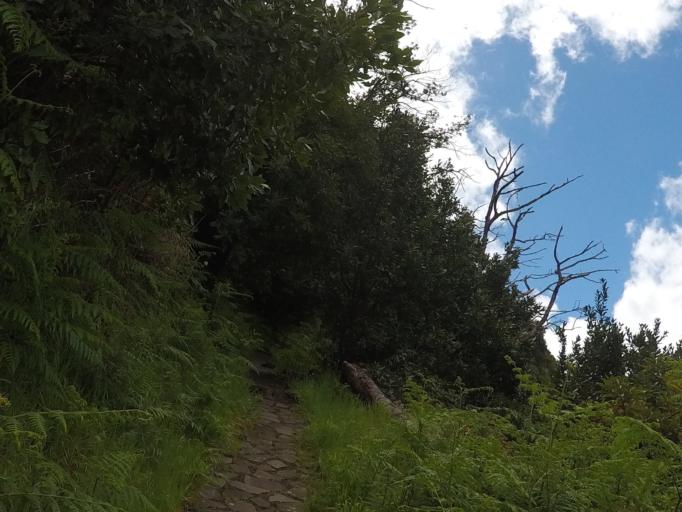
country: PT
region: Madeira
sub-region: Camara de Lobos
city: Curral das Freiras
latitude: 32.7409
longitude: -17.0061
